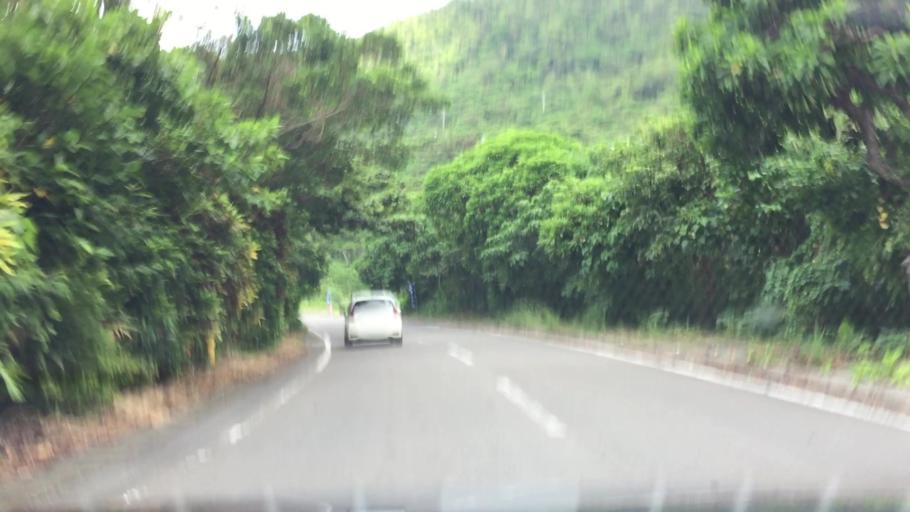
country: JP
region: Okinawa
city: Ishigaki
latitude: 24.4566
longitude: 124.2260
